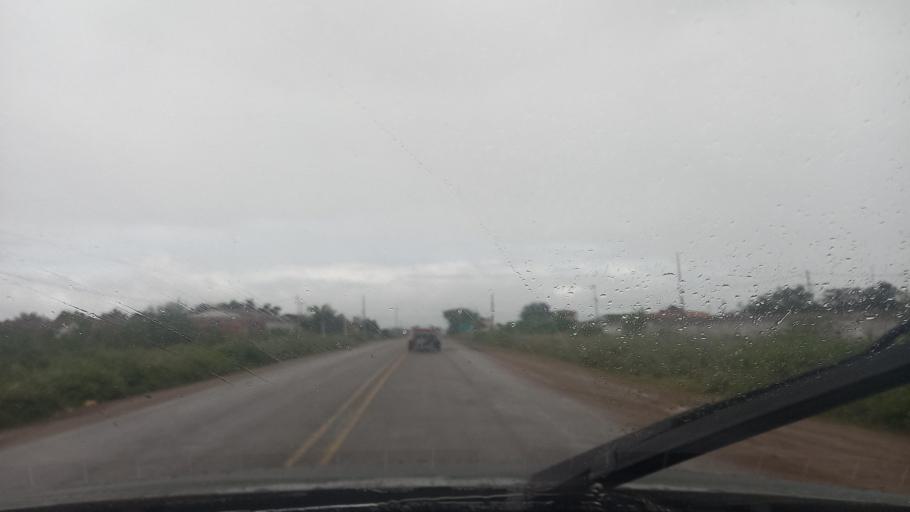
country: BR
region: Bahia
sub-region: Paulo Afonso
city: Paulo Afonso
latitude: -9.3576
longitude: -38.2764
